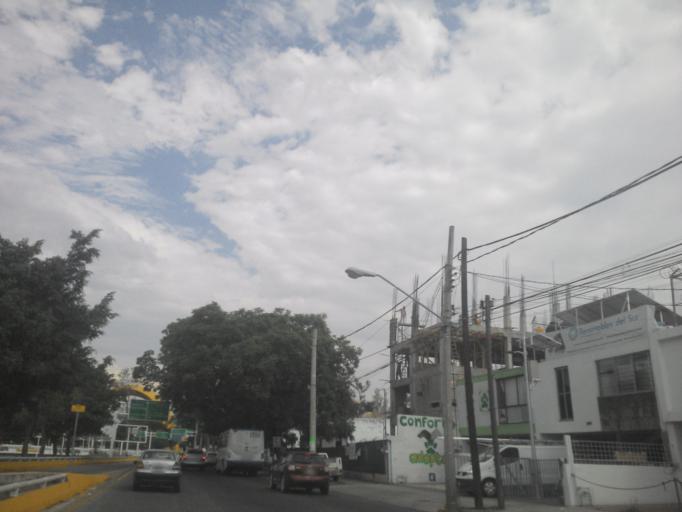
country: MX
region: Jalisco
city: Guadalajara
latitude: 20.6610
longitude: -103.3872
